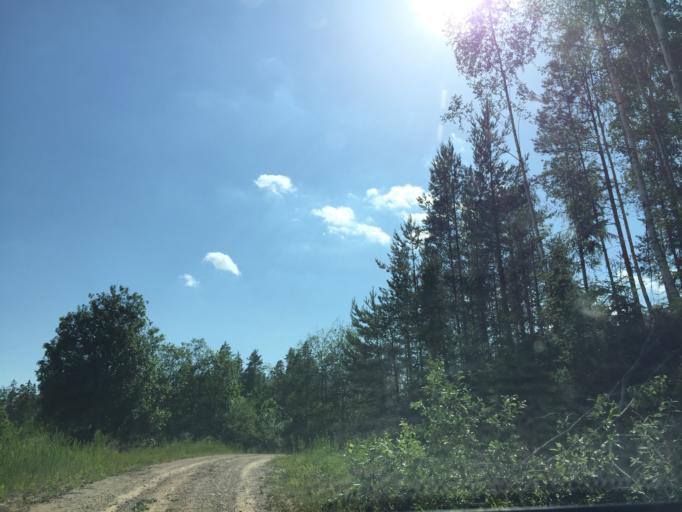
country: LV
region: Tukuma Rajons
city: Tukums
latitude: 57.0187
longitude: 23.2288
